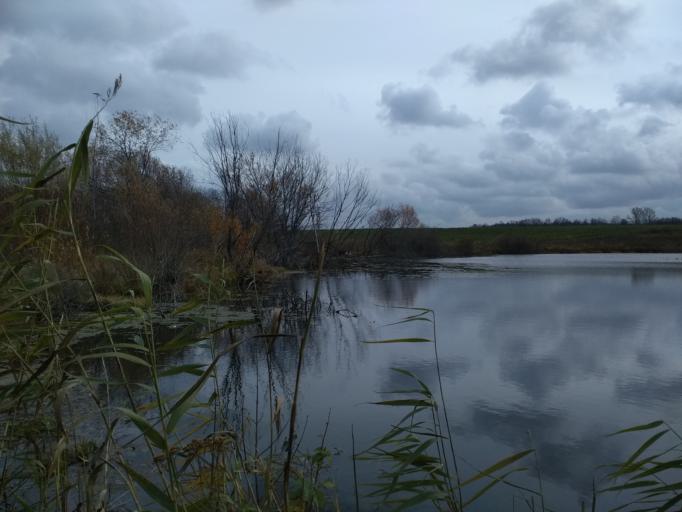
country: RU
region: Bashkortostan
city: Iglino
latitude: 54.7575
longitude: 56.5059
